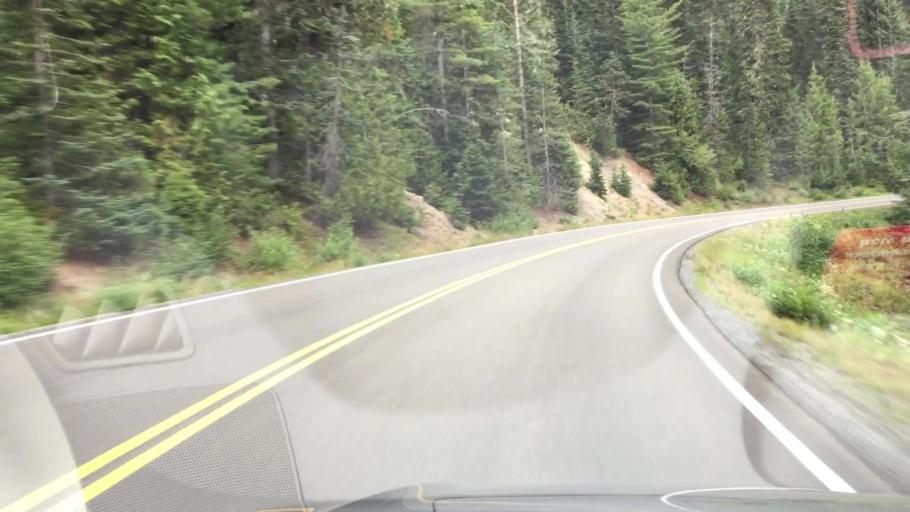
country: US
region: Washington
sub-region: Pierce County
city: Buckley
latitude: 46.7784
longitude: -121.7594
